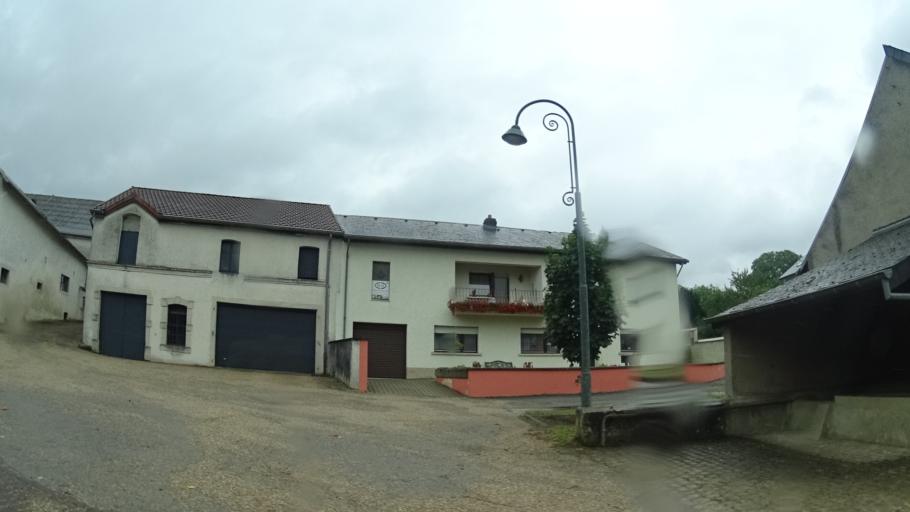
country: LU
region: Grevenmacher
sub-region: Canton de Remich
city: Mondorf-les-Bains
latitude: 49.4863
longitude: 6.3220
